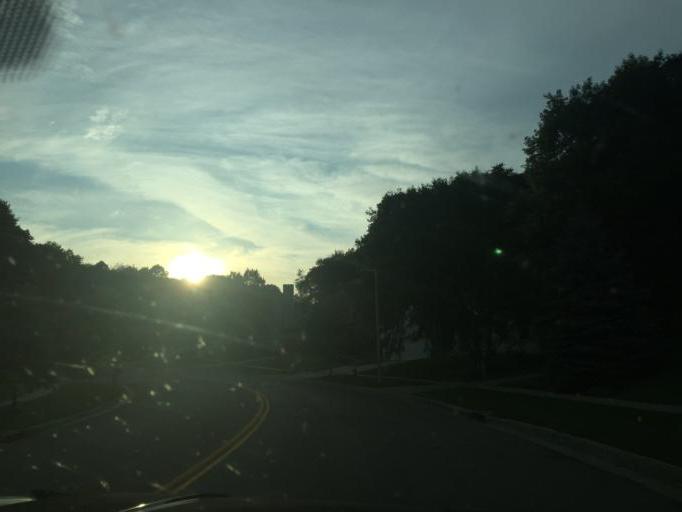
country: US
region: Minnesota
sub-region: Olmsted County
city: Rochester
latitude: 44.0101
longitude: -92.4941
